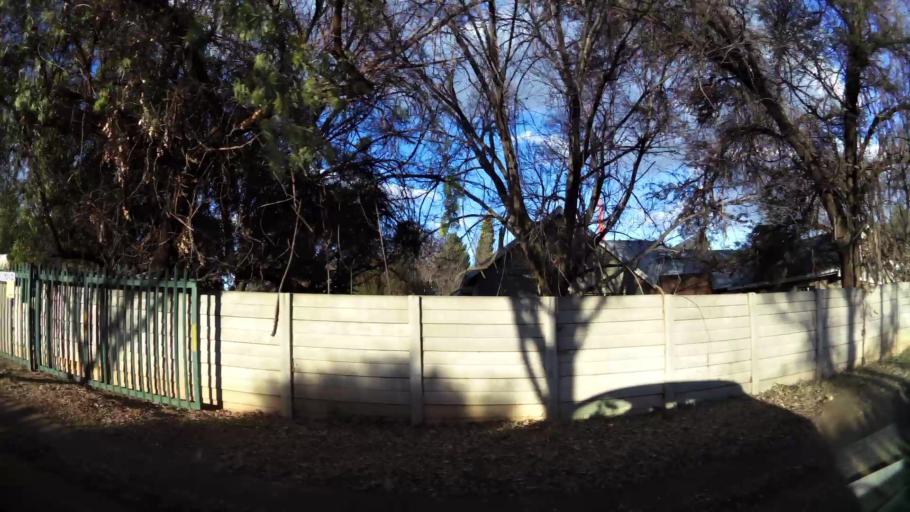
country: ZA
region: North-West
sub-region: Dr Kenneth Kaunda District Municipality
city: Potchefstroom
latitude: -26.6845
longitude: 27.0978
